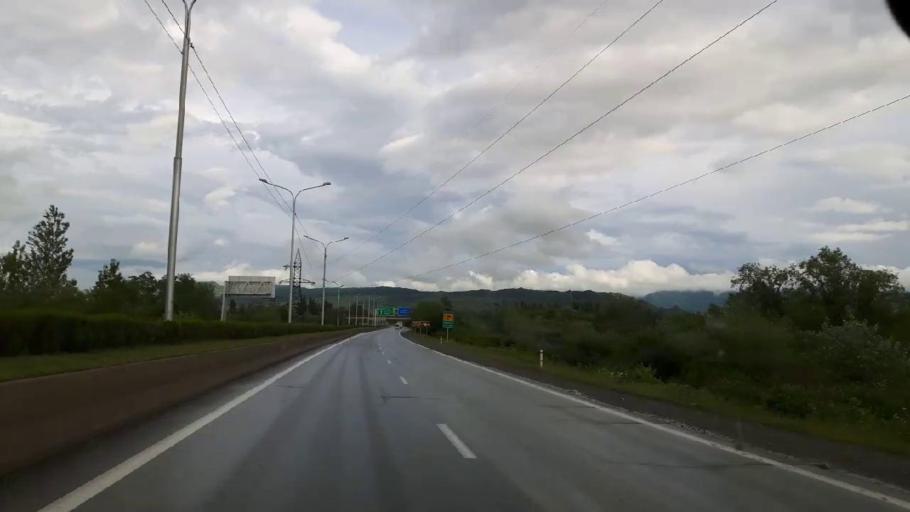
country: GE
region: Shida Kartli
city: Kaspi
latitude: 41.9155
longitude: 44.5557
